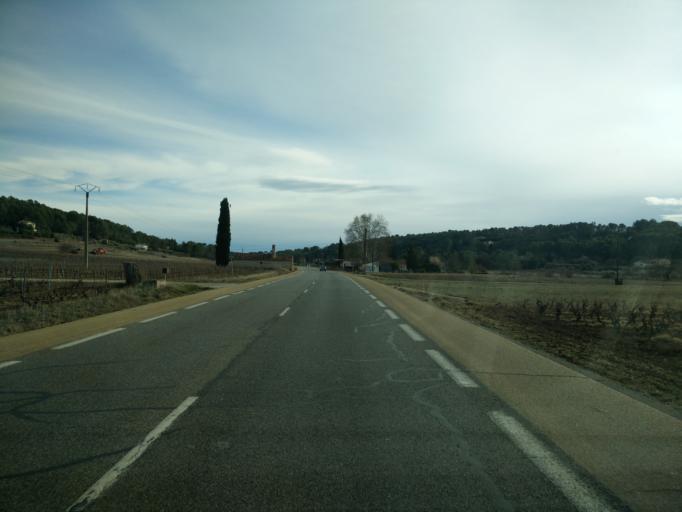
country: FR
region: Provence-Alpes-Cote d'Azur
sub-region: Departement du Var
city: Lorgues
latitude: 43.4781
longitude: 6.3729
